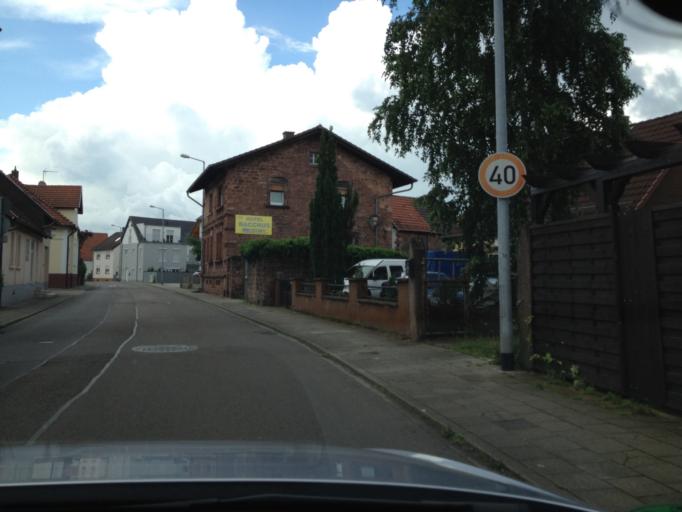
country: DE
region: Rheinland-Pfalz
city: Ramstein-Miesenbach
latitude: 49.4427
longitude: 7.5612
